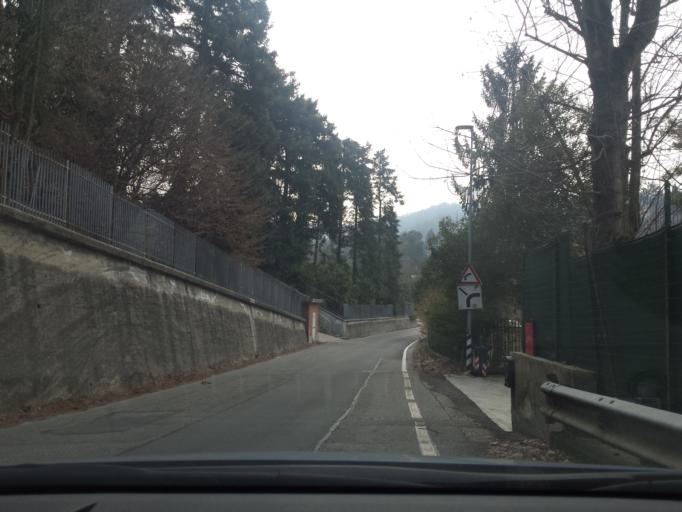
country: IT
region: Piedmont
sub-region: Provincia di Torino
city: Turin
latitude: 45.0550
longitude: 7.7219
